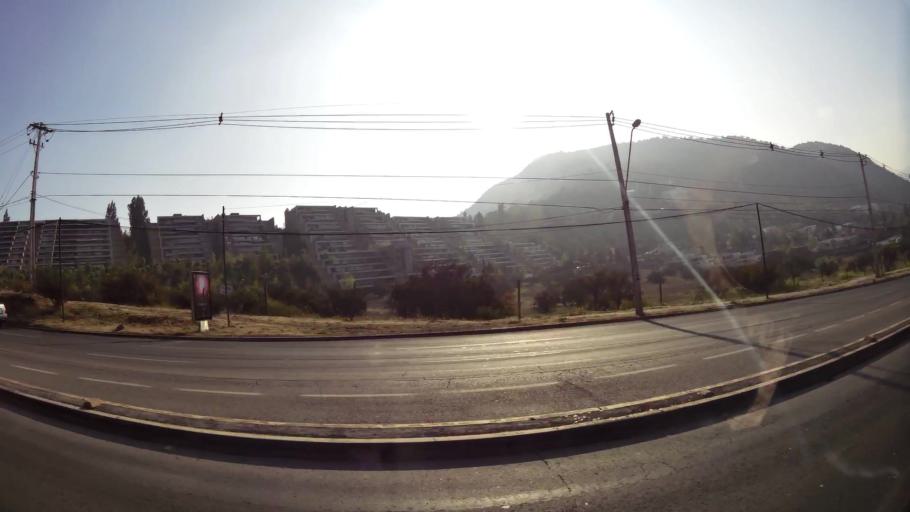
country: CL
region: Santiago Metropolitan
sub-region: Provincia de Santiago
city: Villa Presidente Frei, Nunoa, Santiago, Chile
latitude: -33.3641
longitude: -70.5446
